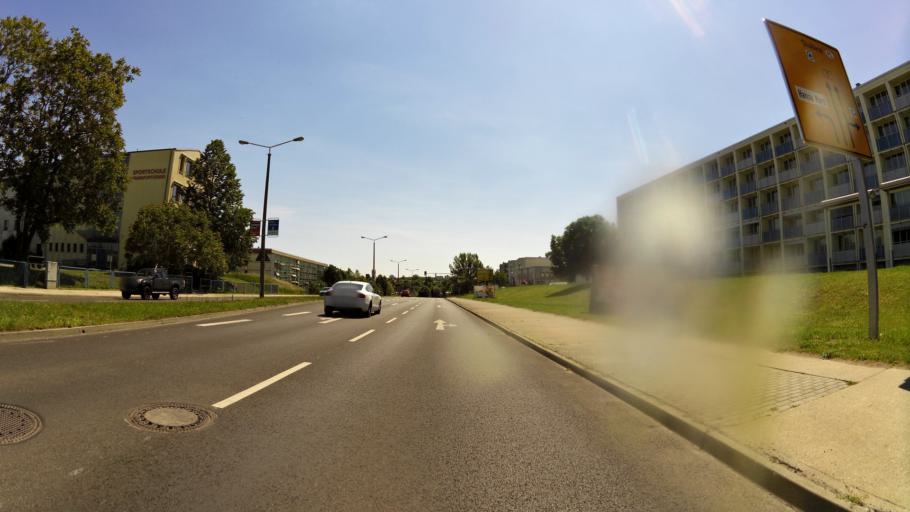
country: DE
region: Brandenburg
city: Frankfurt (Oder)
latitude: 52.3559
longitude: 14.5312
